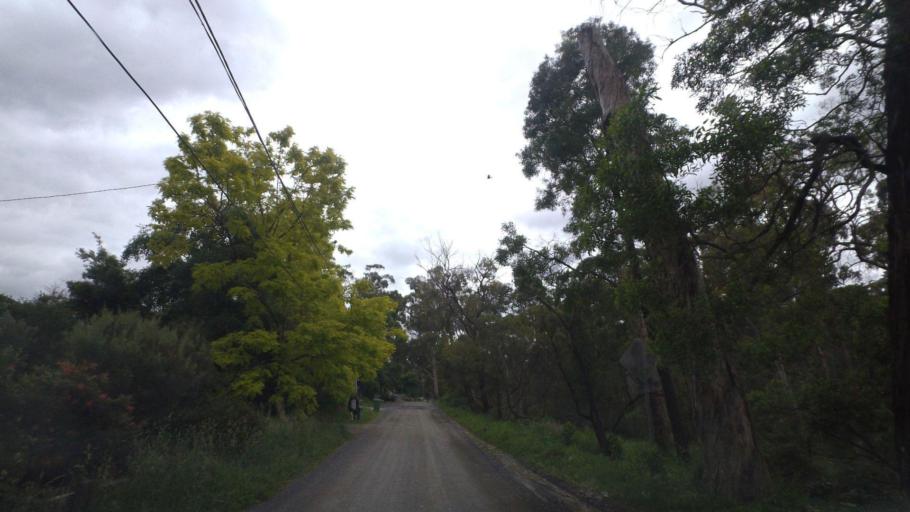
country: AU
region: Victoria
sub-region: Yarra Ranges
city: Mount Evelyn
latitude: -37.7902
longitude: 145.3659
